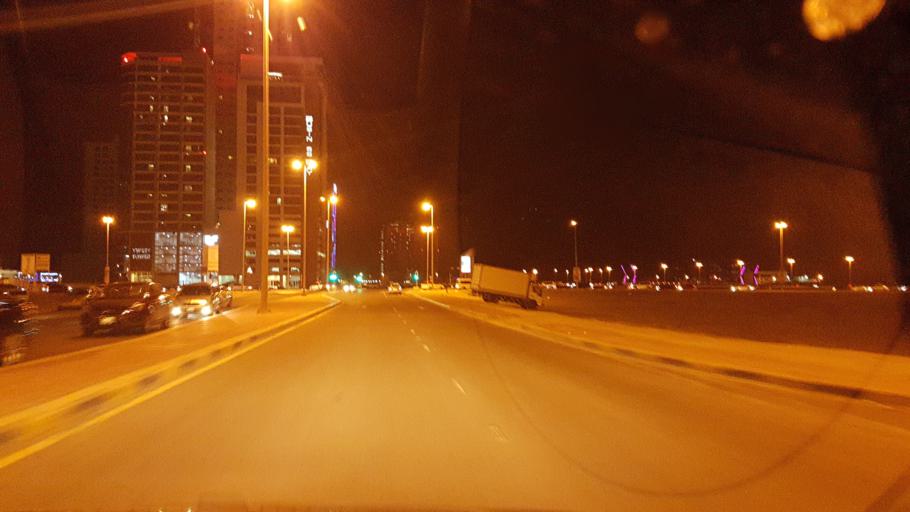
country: BH
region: Manama
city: Jidd Hafs
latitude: 26.2337
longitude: 50.5573
